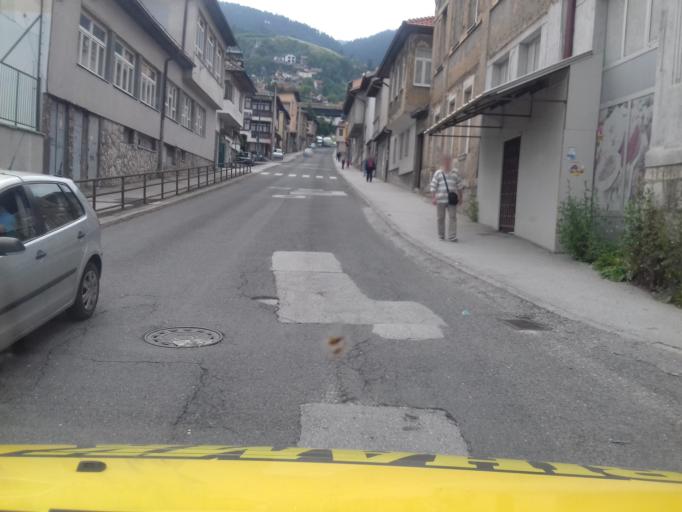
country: BA
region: Federation of Bosnia and Herzegovina
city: Kobilja Glava
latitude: 43.8540
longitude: 18.4303
